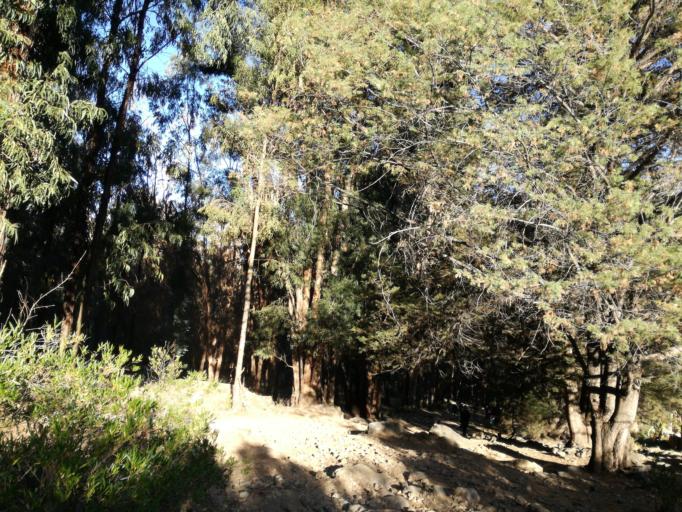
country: BO
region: Cochabamba
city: Sipe Sipe
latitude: -17.3422
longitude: -66.3329
